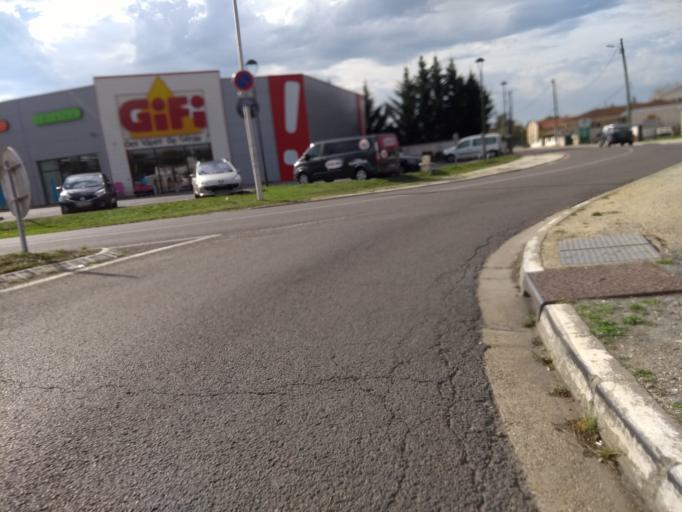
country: FR
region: Aquitaine
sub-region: Departement de la Gironde
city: Cestas
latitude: 44.7821
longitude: -0.6889
